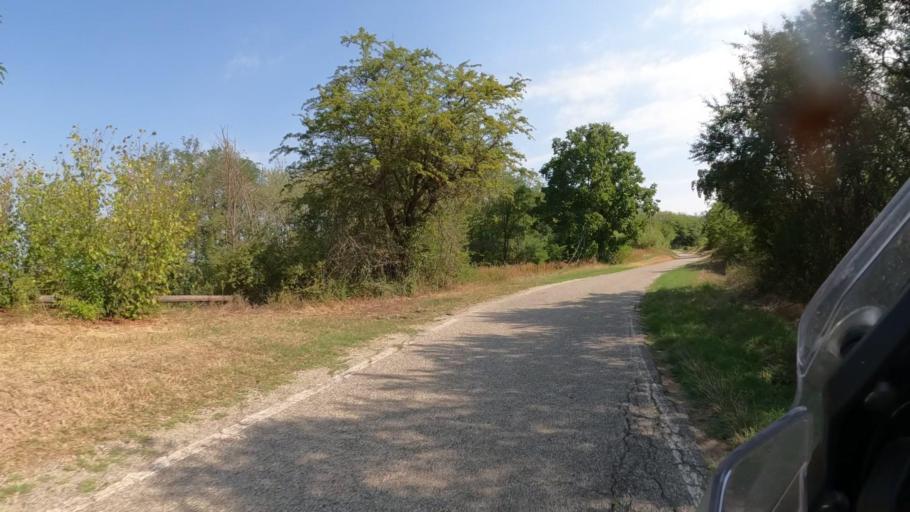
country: IT
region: Piedmont
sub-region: Provincia di Asti
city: Viarigi
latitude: 44.9607
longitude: 8.3786
